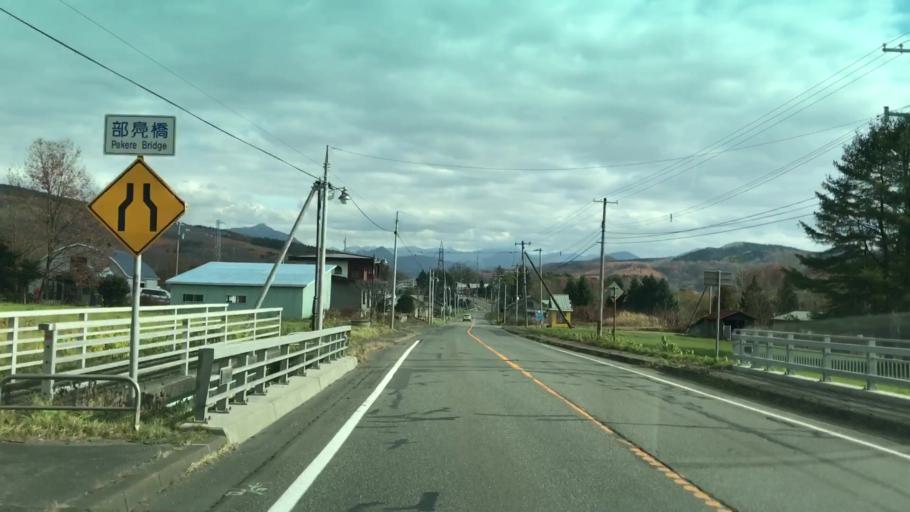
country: JP
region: Hokkaido
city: Shizunai-furukawacho
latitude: 42.7258
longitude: 142.2882
